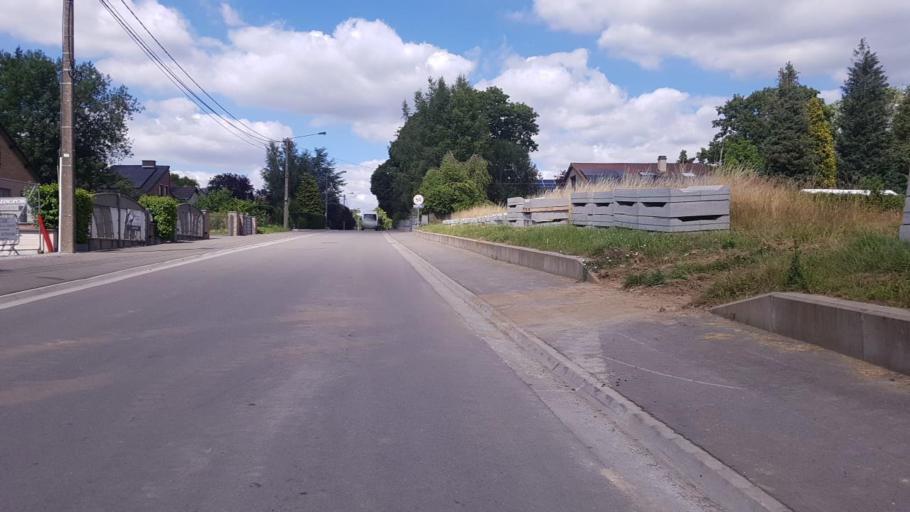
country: BE
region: Wallonia
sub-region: Province du Hainaut
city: Thuin
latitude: 50.3247
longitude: 4.3777
